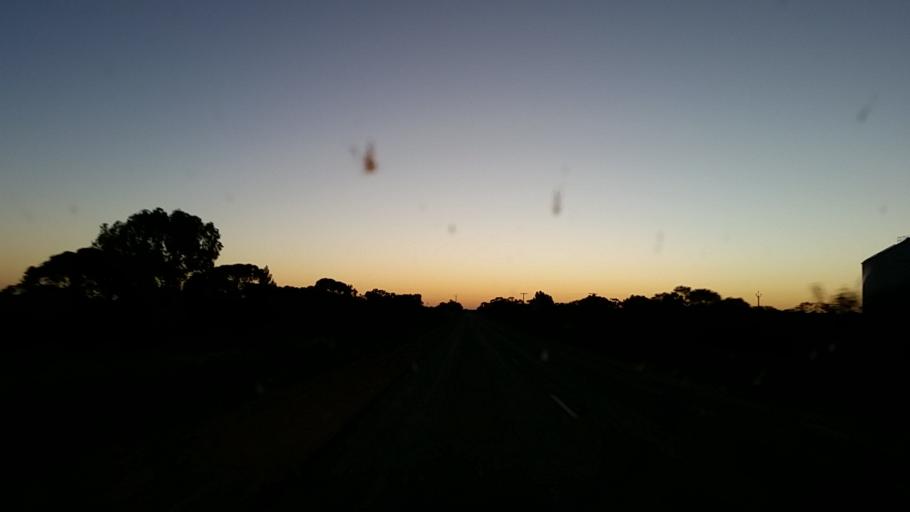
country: AU
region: South Australia
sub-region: Wakefield
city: Balaklava
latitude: -34.1241
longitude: 138.4635
